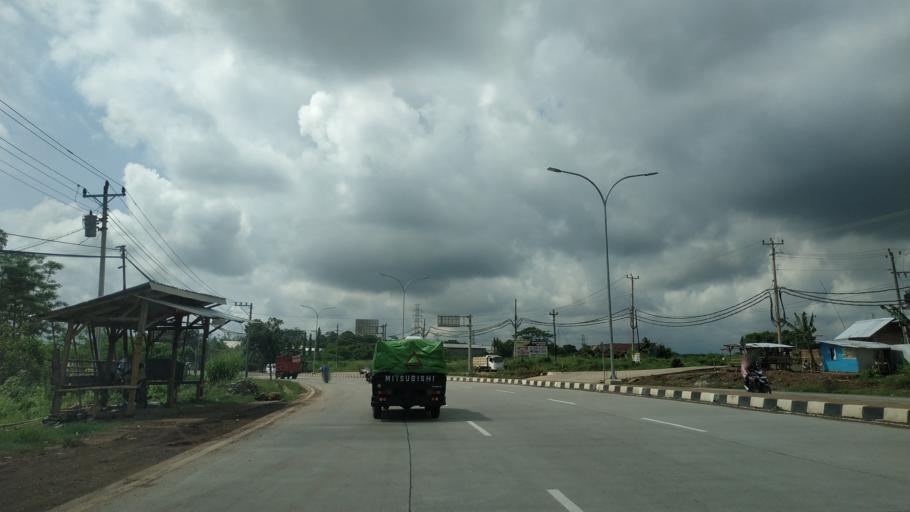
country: ID
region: Central Java
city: Pekalongan
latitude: -6.9319
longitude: 109.7652
